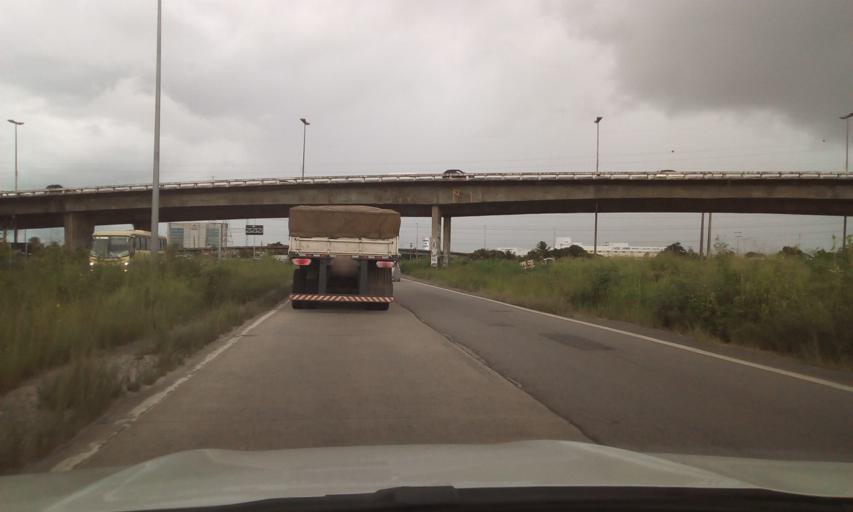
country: BR
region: Pernambuco
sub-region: Recife
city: Recife
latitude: -8.0661
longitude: -34.9427
